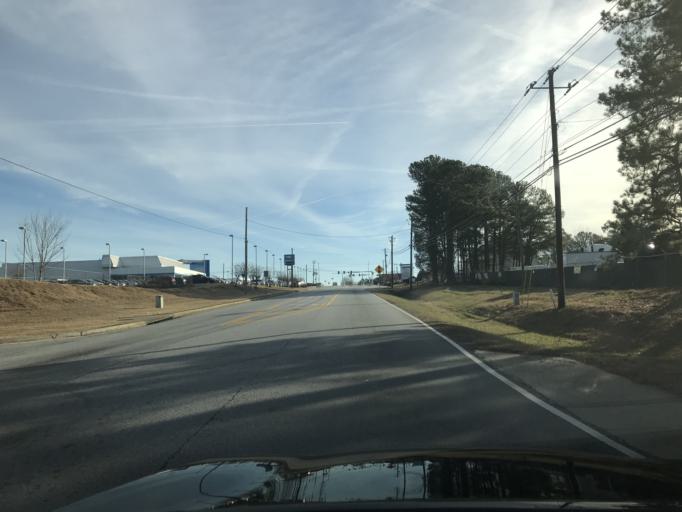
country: US
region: Georgia
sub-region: Clayton County
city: Jonesboro
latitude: 33.5532
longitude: -84.3503
